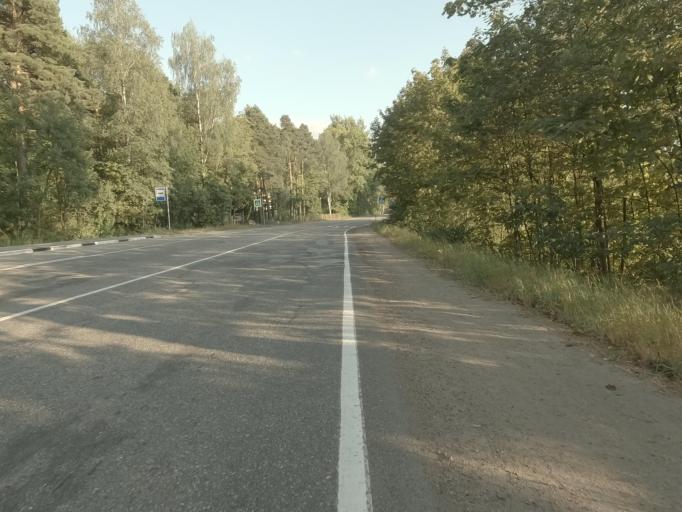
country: RU
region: Leningrad
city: Vyborg
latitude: 60.7325
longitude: 28.7589
